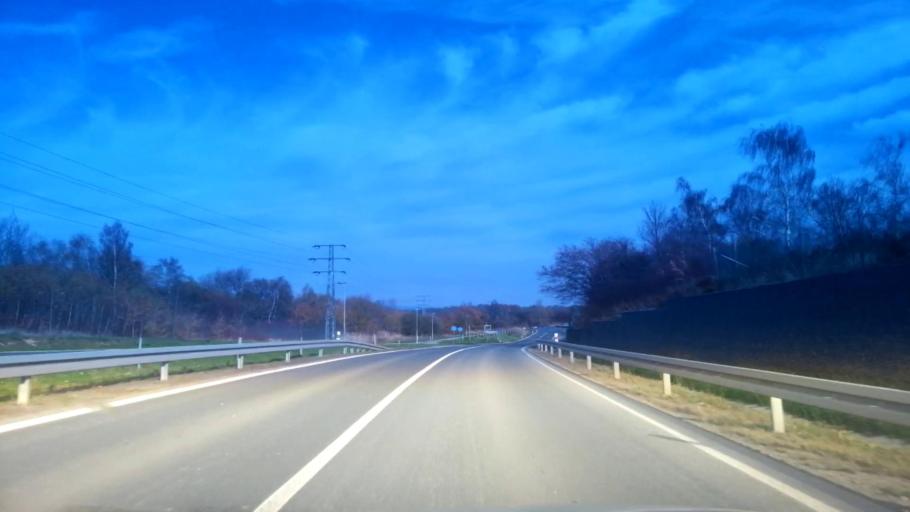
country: CZ
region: Karlovarsky
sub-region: Okres Cheb
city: Cheb
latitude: 50.0669
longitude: 12.3853
